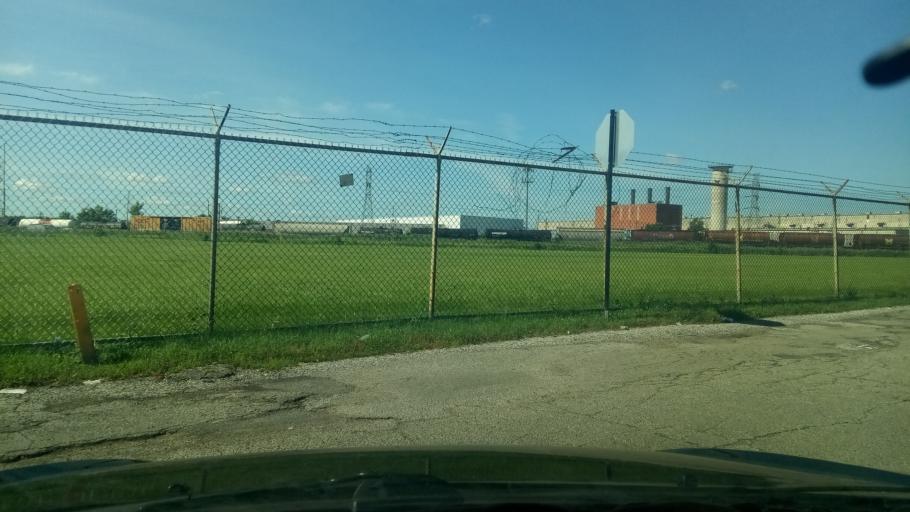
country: US
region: Illinois
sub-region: Cook County
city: Hometown
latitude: 41.7612
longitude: -87.7162
